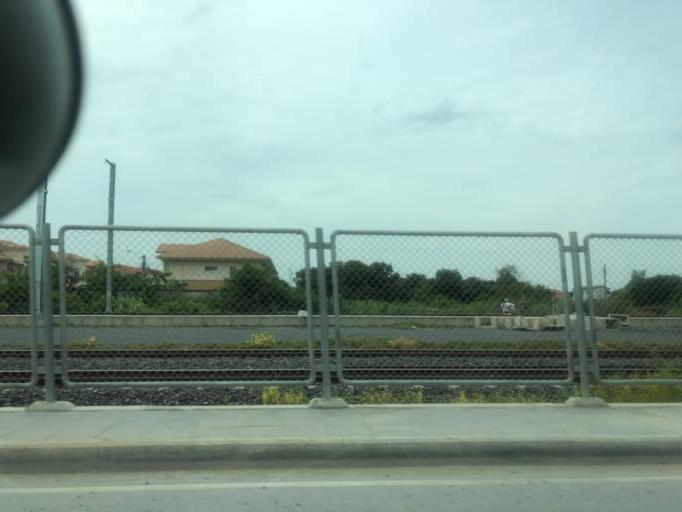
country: TH
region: Bangkok
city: Don Mueang
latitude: 13.9494
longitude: 100.6071
